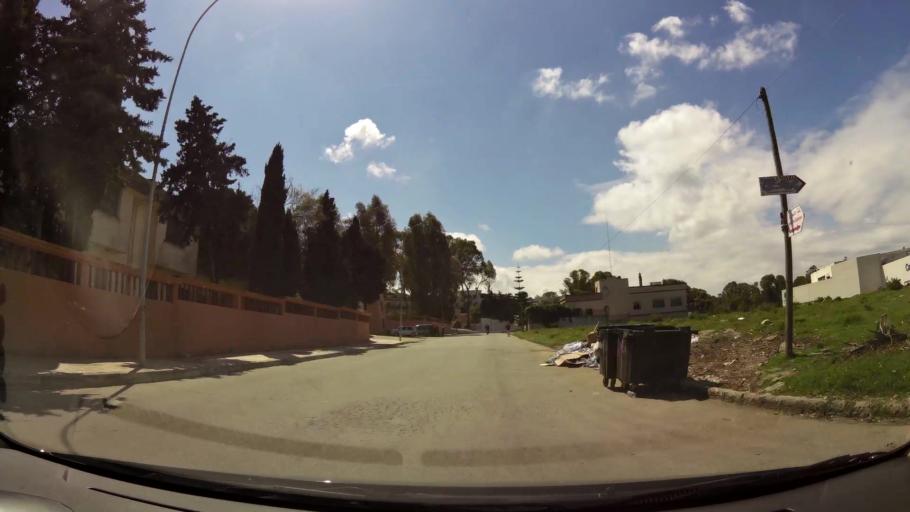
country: MA
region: Tanger-Tetouan
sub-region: Tanger-Assilah
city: Tangier
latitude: 35.7815
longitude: -5.8382
